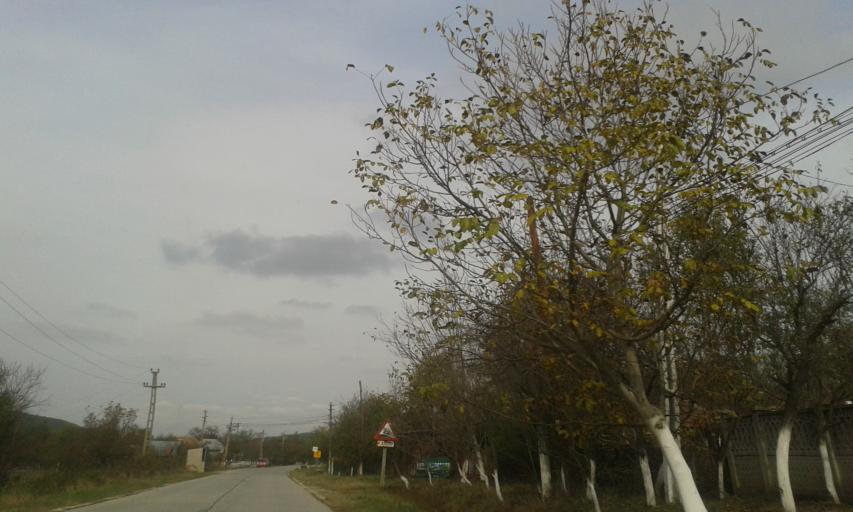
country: RO
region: Gorj
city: Logresti
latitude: 44.8649
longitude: 23.7017
